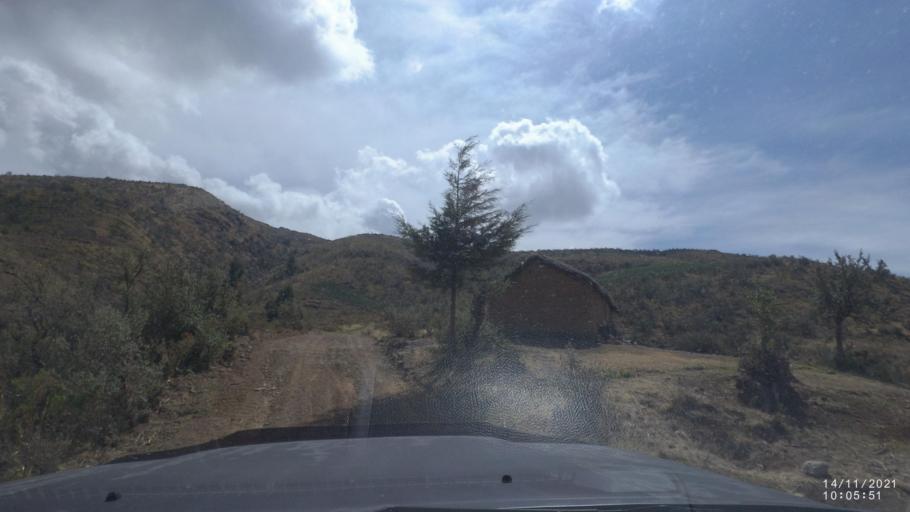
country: BO
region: Cochabamba
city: Cochabamba
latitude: -17.3483
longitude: -66.0909
